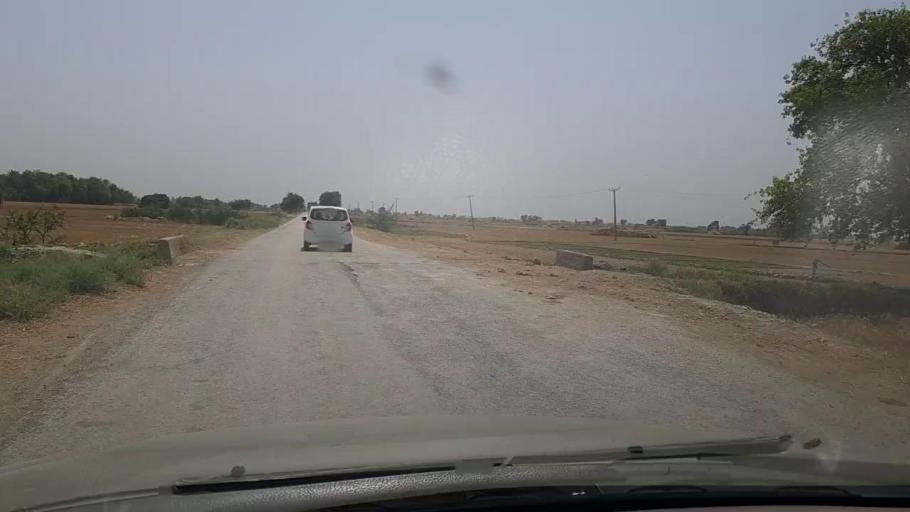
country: PK
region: Sindh
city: Miro Khan
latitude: 27.7230
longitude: 68.0697
